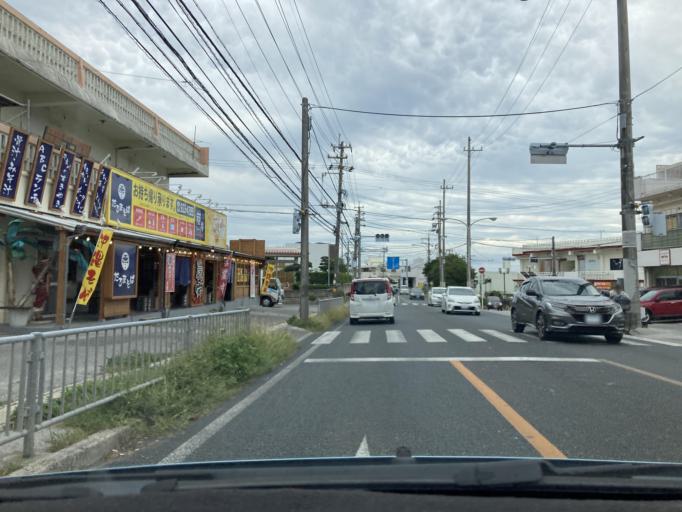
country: JP
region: Okinawa
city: Okinawa
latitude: 26.3839
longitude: 127.7416
